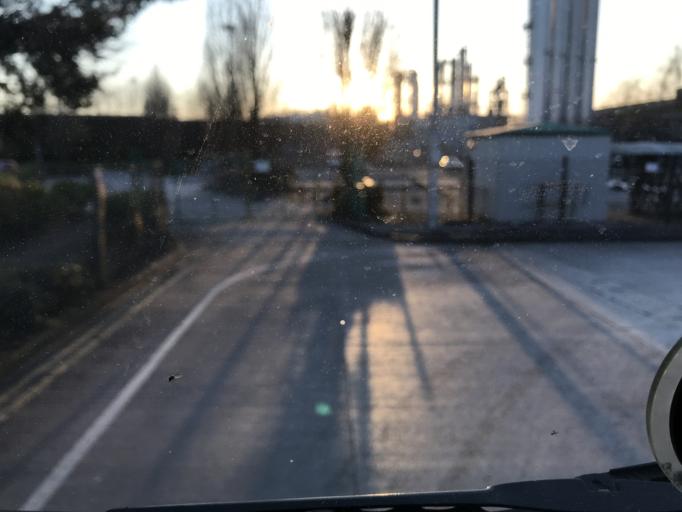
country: GB
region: England
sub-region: City and Borough of Salford
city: Eccles
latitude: 53.4775
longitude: -2.3293
